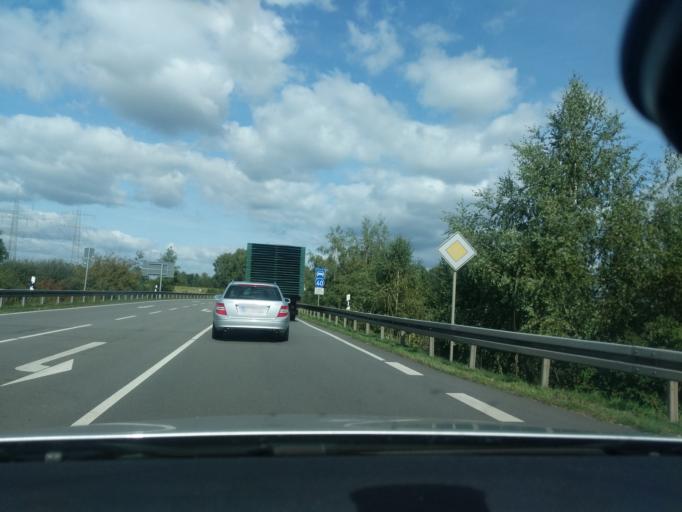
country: DE
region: Lower Saxony
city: Bohmte
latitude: 52.3577
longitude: 8.2979
